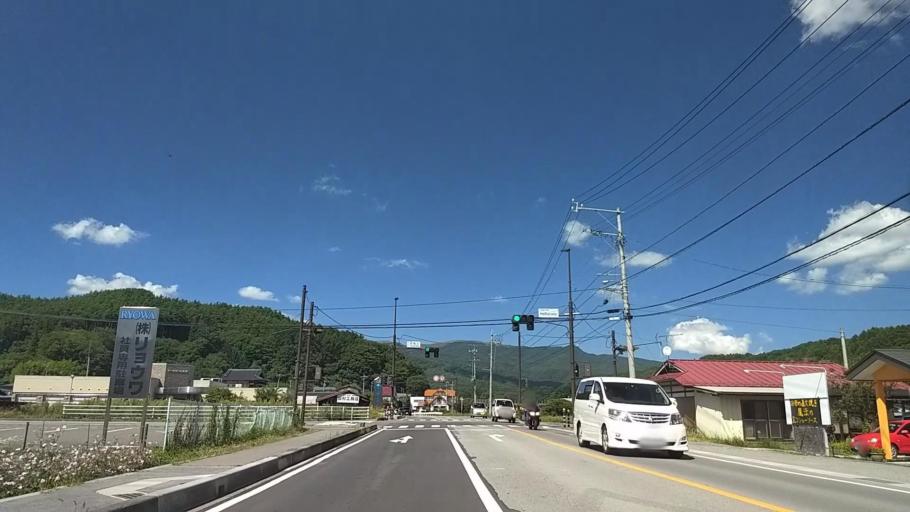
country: JP
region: Nagano
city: Chino
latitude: 36.0139
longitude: 138.1758
